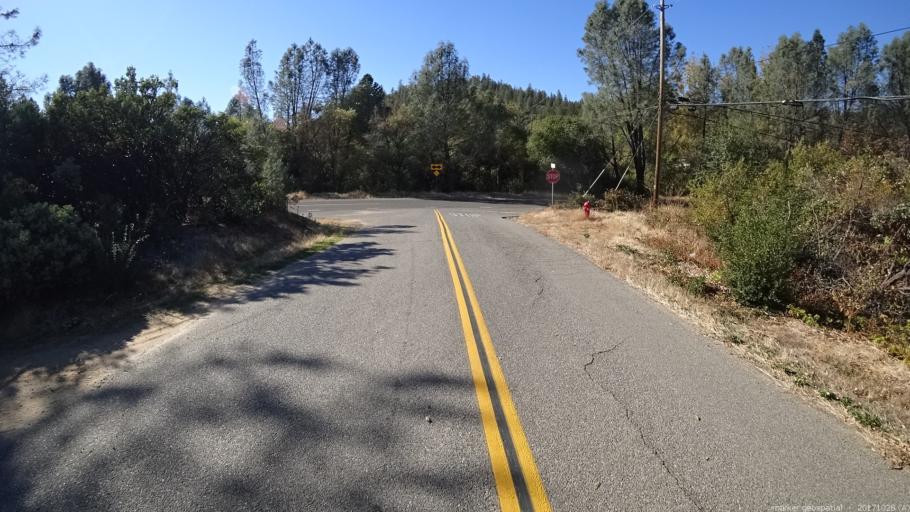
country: US
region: California
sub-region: Shasta County
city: Shasta
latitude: 40.6226
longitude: -122.4661
